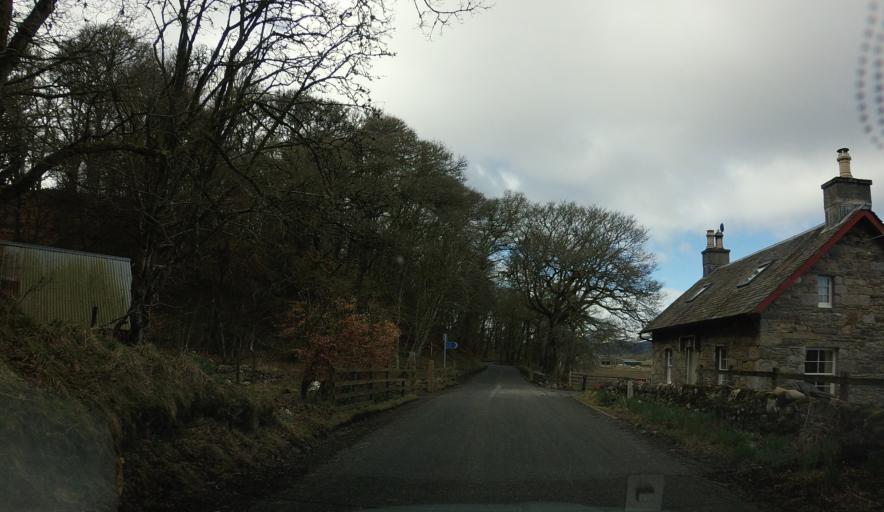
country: GB
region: Scotland
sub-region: Perth and Kinross
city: Pitlochry
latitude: 56.6444
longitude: -3.6849
